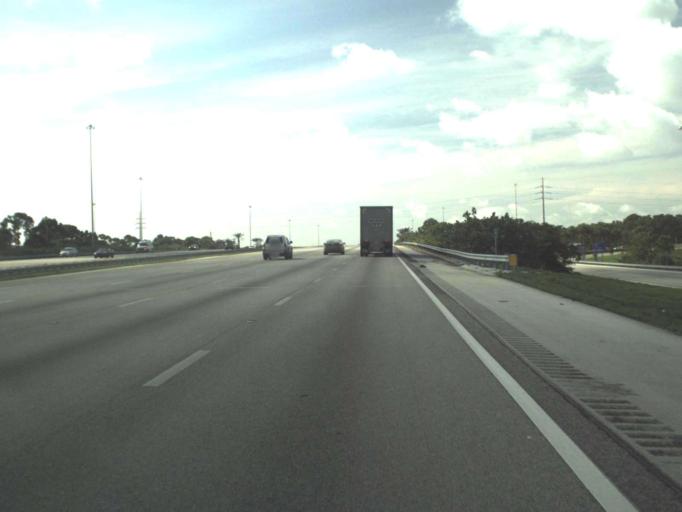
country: US
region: Florida
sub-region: Palm Beach County
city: Limestone Creek
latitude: 26.8865
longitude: -80.1307
